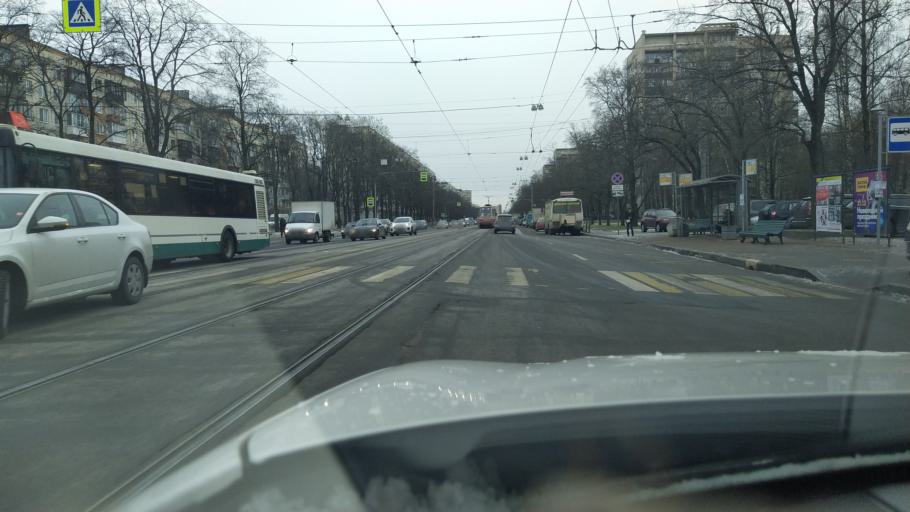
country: RU
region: Leningrad
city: Akademicheskoe
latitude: 60.0103
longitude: 30.4086
